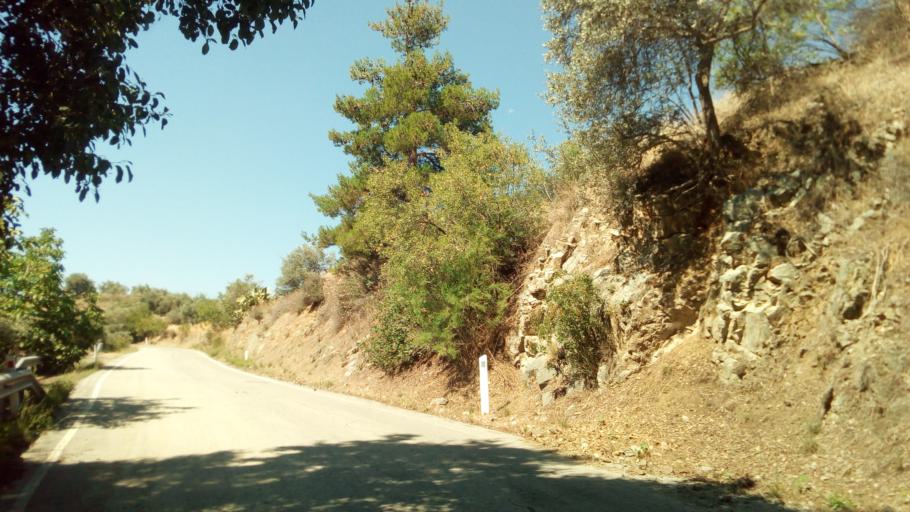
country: CY
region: Limassol
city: Parekklisha
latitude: 34.8682
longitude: 33.1798
